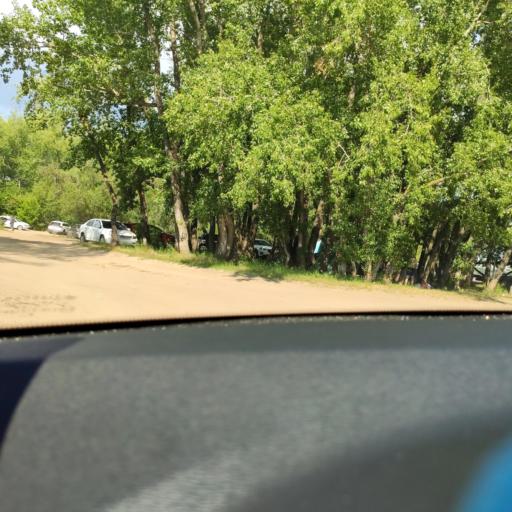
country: RU
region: Samara
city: Volzhskiy
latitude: 53.4320
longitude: 50.1660
